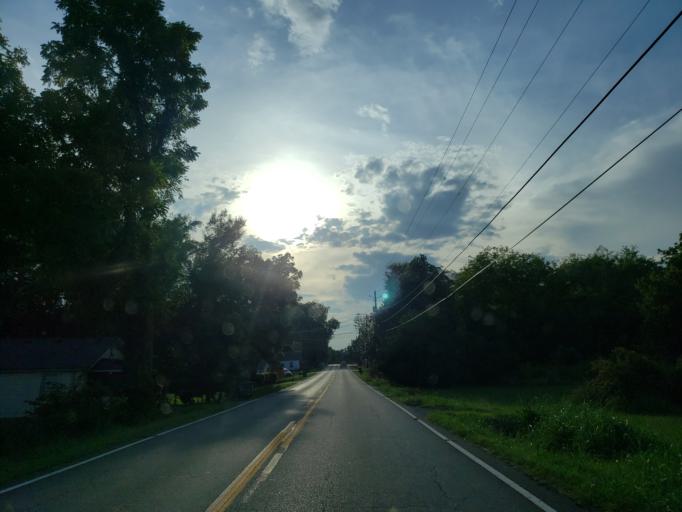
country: US
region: Georgia
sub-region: Bartow County
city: Euharlee
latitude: 34.2379
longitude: -84.9408
